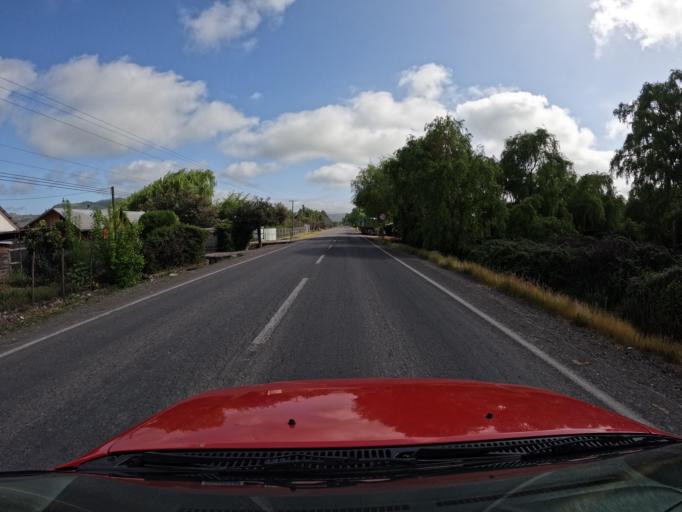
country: CL
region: Maule
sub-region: Provincia de Curico
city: Teno
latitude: -34.8581
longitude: -71.1912
